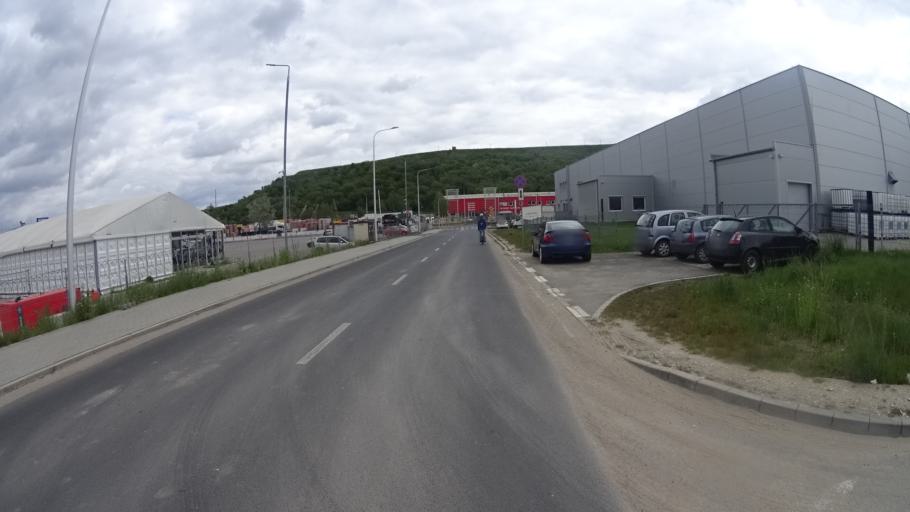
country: PL
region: Masovian Voivodeship
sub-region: Powiat warszawski zachodni
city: Babice
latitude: 52.2772
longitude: 20.8739
